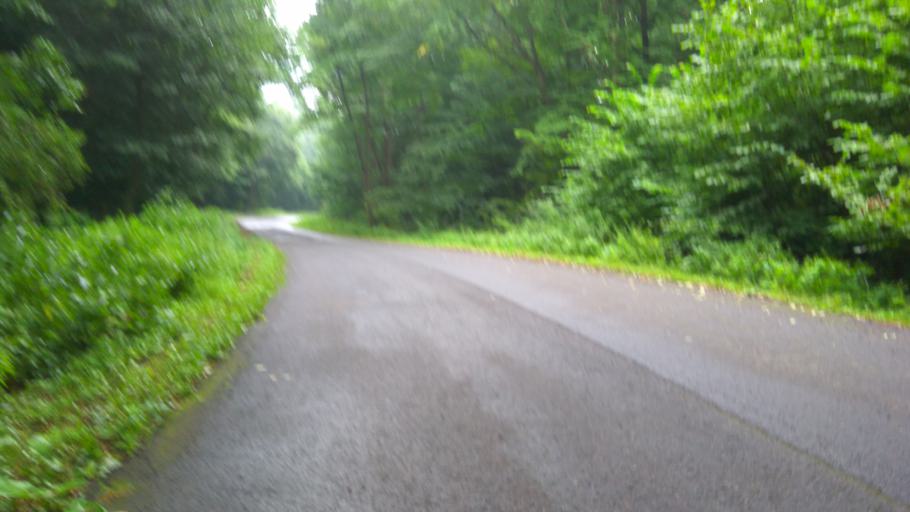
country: HU
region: Nograd
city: Diosjeno
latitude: 47.9849
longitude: 18.9735
